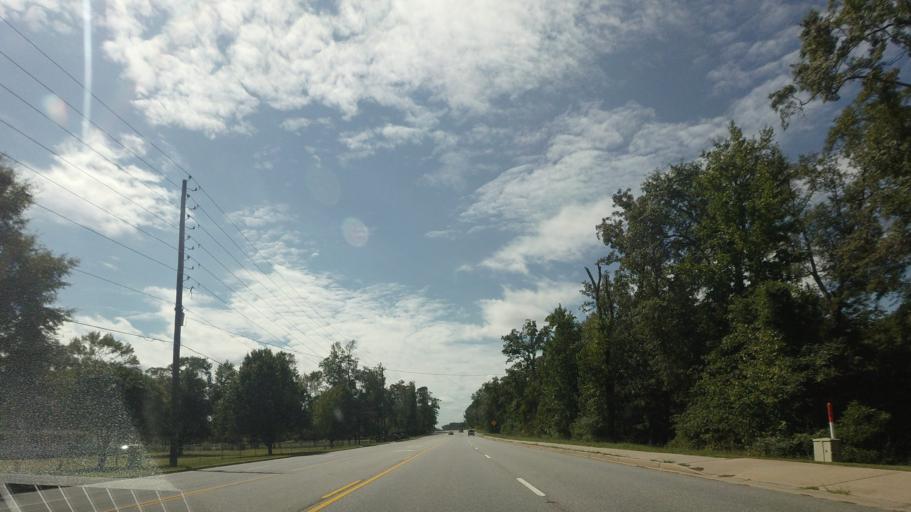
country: US
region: Georgia
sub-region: Houston County
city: Centerville
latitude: 32.5570
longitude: -83.6913
